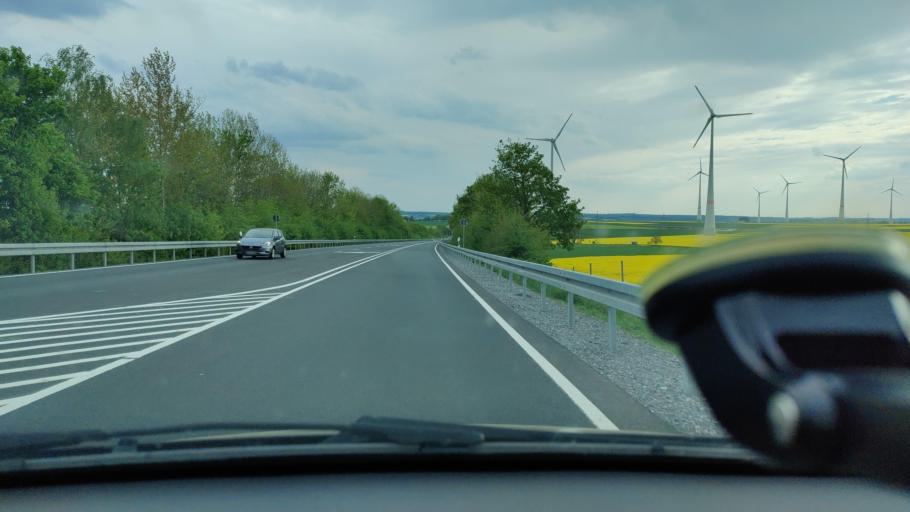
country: DE
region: North Rhine-Westphalia
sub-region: Regierungsbezirk Detmold
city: Wunnenberg
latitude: 51.5486
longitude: 8.7143
